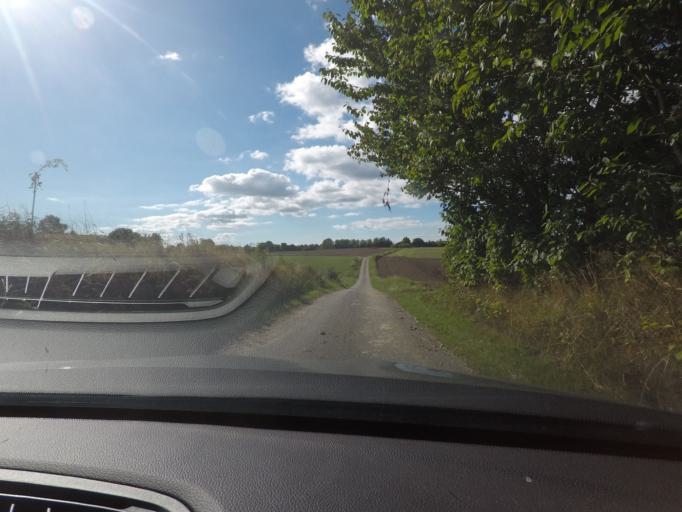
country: DK
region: Zealand
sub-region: Guldborgsund Kommune
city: Sakskobing
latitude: 54.9693
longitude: 11.5445
